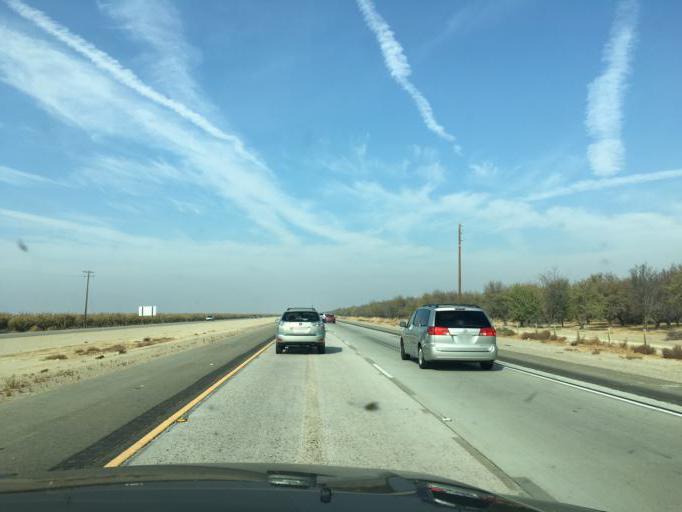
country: US
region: California
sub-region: Kern County
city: Buttonwillow
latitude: 35.5130
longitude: -119.5487
